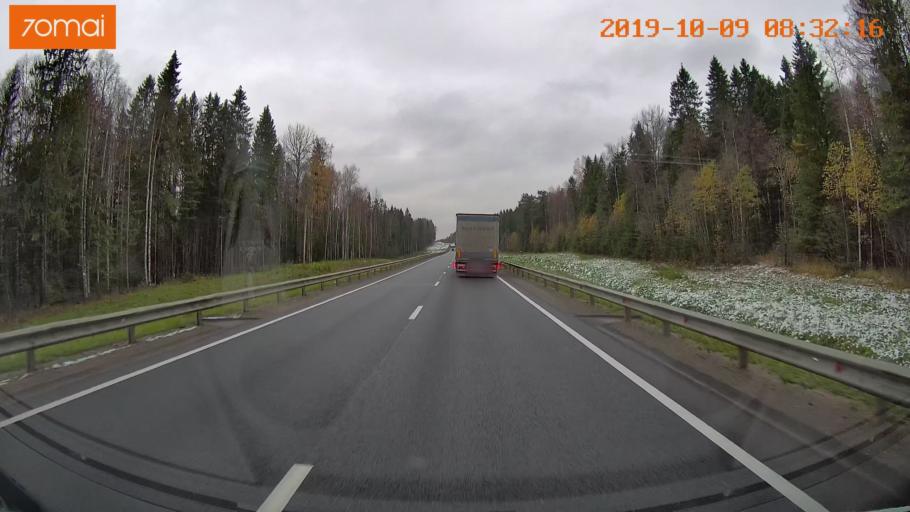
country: RU
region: Vologda
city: Gryazovets
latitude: 58.8645
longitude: 40.1981
